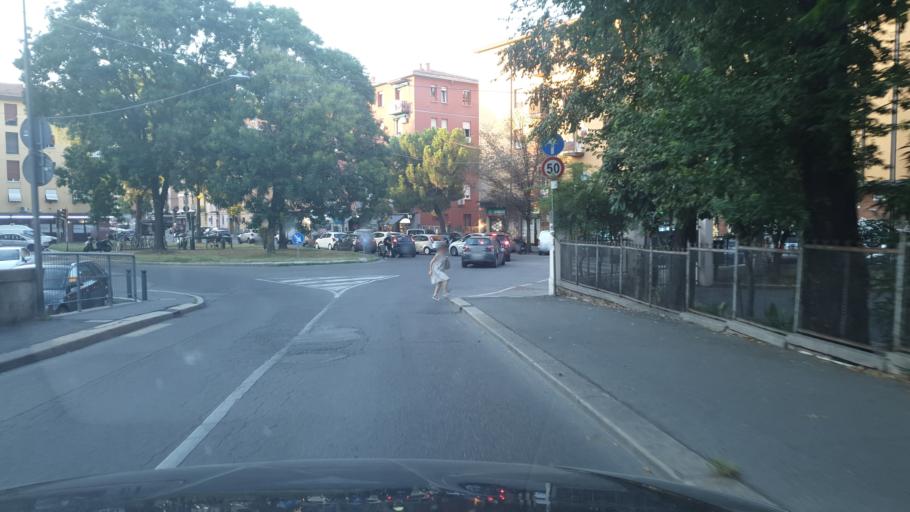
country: IT
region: Emilia-Romagna
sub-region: Provincia di Bologna
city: Bologna
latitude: 44.5013
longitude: 11.3654
